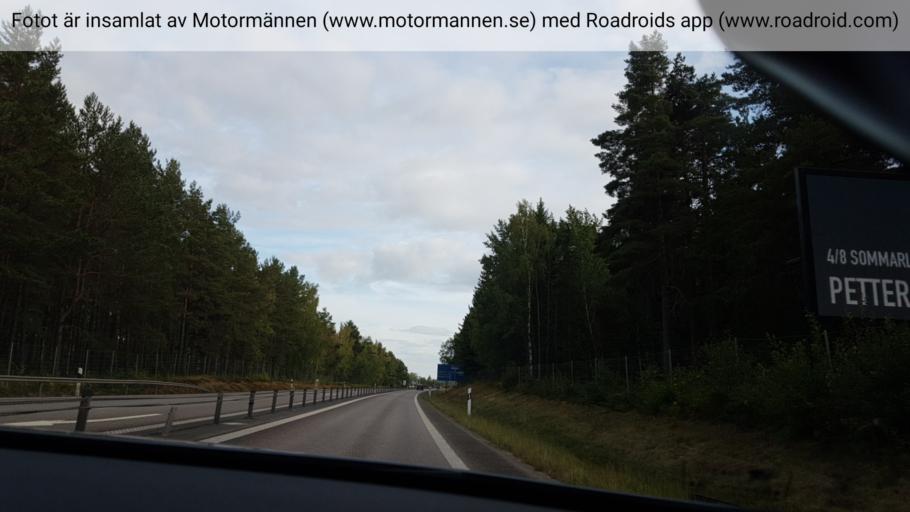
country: SE
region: Vaestra Goetaland
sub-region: Skovde Kommun
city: Skoevde
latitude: 58.4252
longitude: 13.8664
